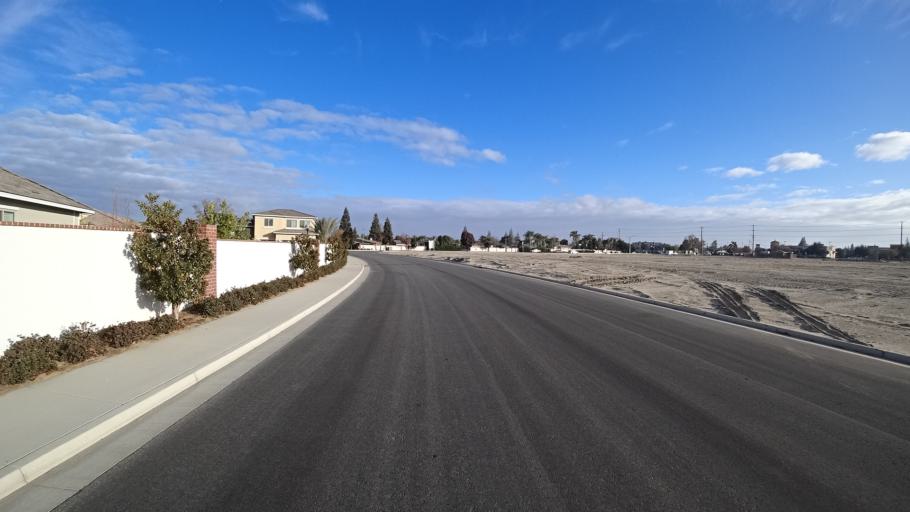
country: US
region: California
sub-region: Kern County
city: Rosedale
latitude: 35.3243
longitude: -119.1305
